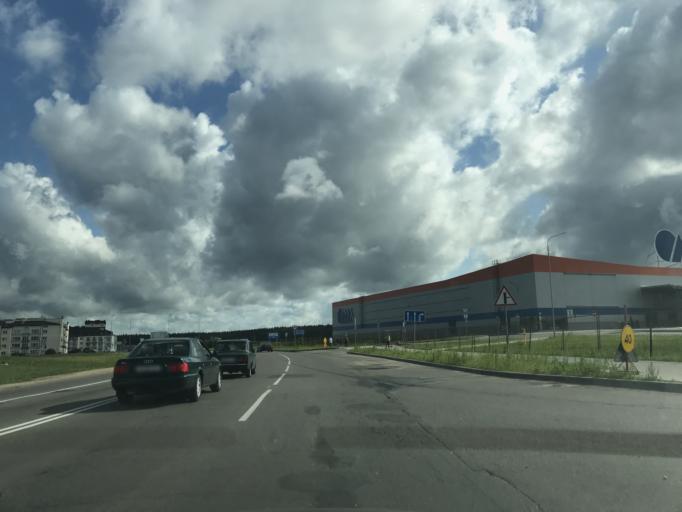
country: BY
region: Minsk
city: Borovlyany
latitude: 53.9665
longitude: 27.6227
